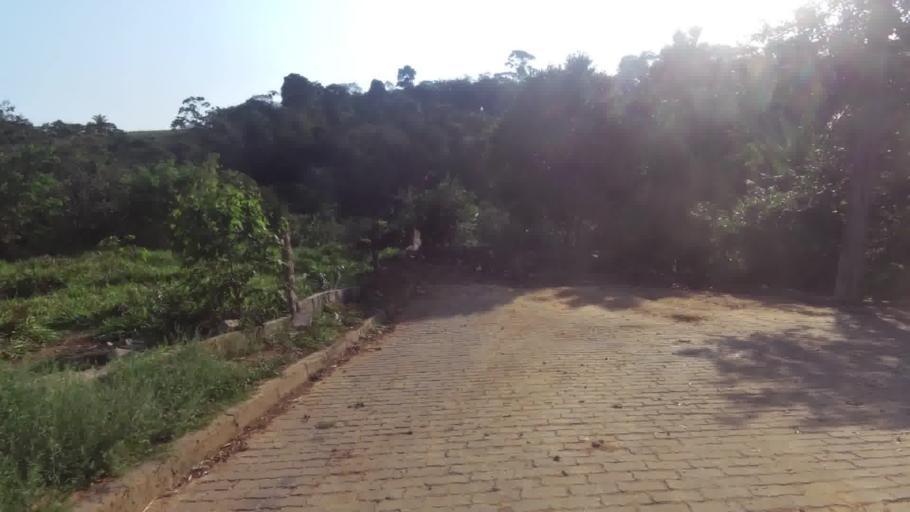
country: BR
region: Espirito Santo
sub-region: Piuma
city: Piuma
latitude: -20.8239
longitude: -40.7221
